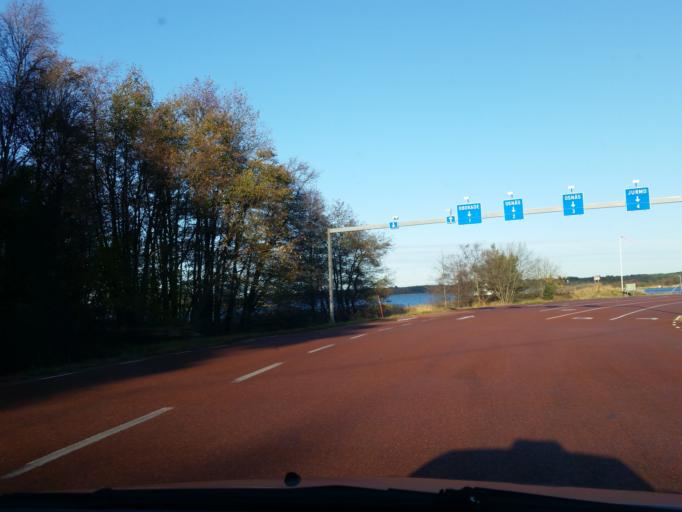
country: AX
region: Alands skaergard
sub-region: Braendoe
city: Braendoe
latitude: 60.5021
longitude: 21.0551
